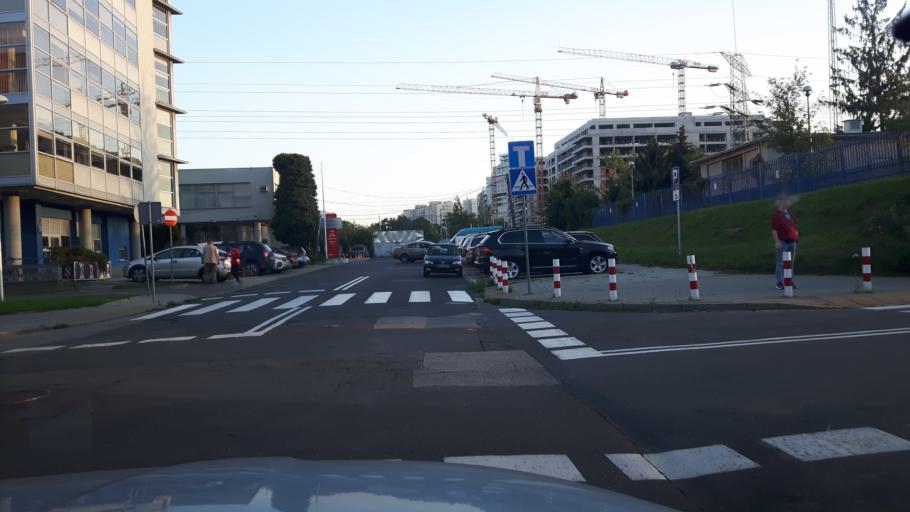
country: PL
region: Masovian Voivodeship
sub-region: Warszawa
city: Zoliborz
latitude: 52.2605
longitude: 20.9891
